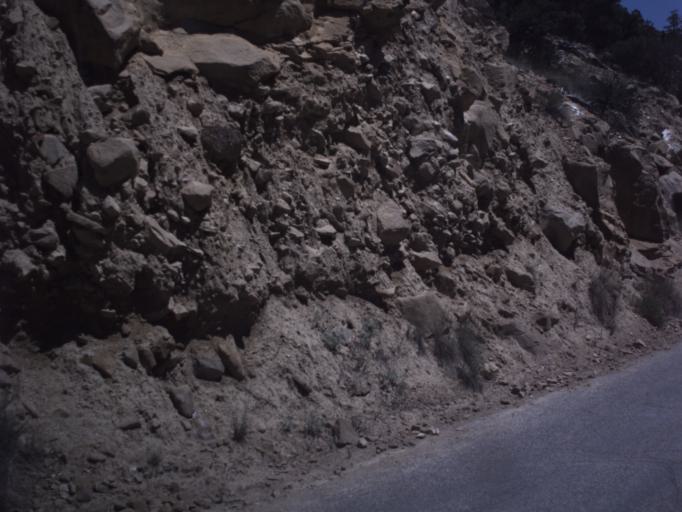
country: US
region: Utah
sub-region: Emery County
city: Orangeville
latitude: 39.2811
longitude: -111.2312
